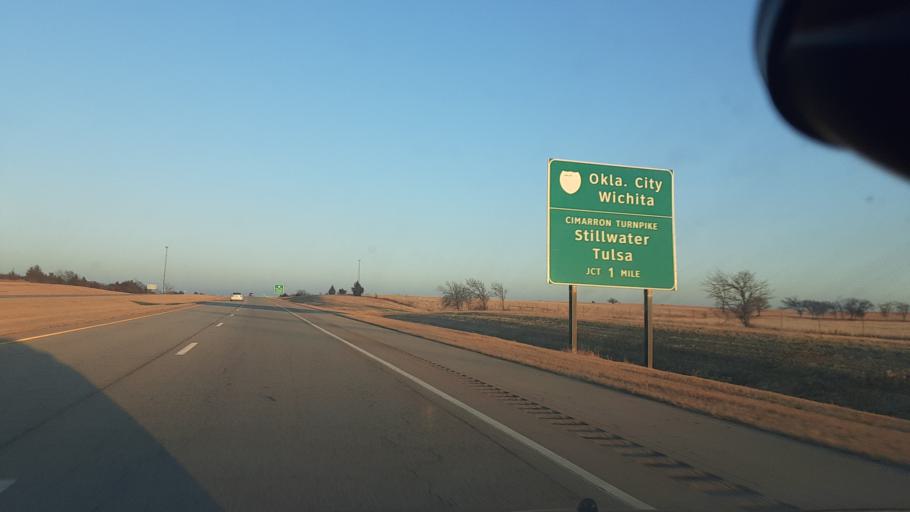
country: US
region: Oklahoma
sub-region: Noble County
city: Perry
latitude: 36.3984
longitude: -97.3509
